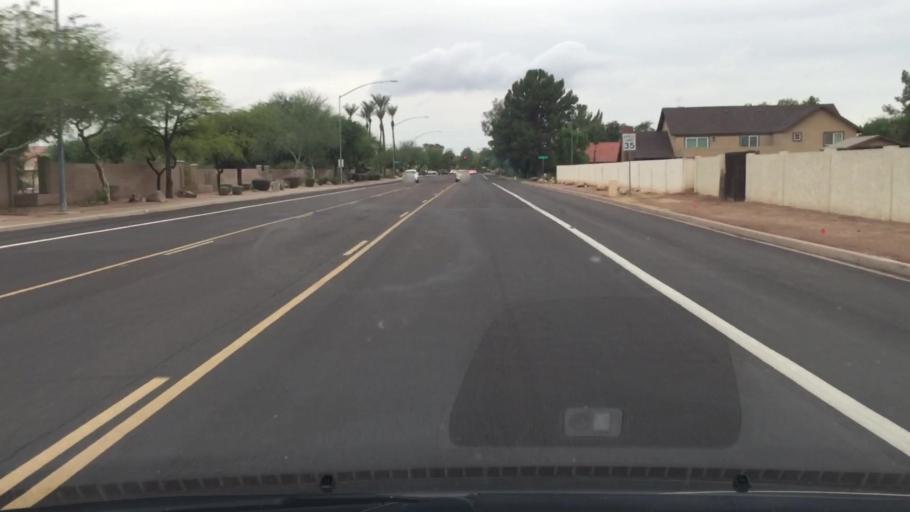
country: US
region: Arizona
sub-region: Maricopa County
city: Gilbert
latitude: 33.3823
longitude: -111.7627
